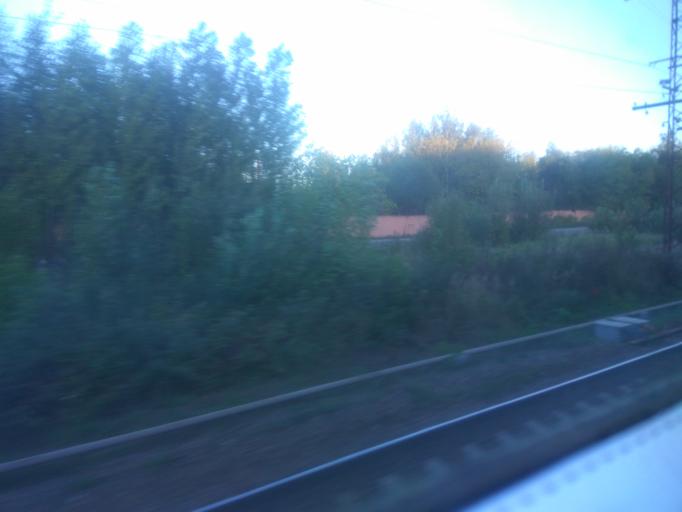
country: RU
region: Moskovskaya
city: Elektrostal'
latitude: 55.7827
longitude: 38.4626
